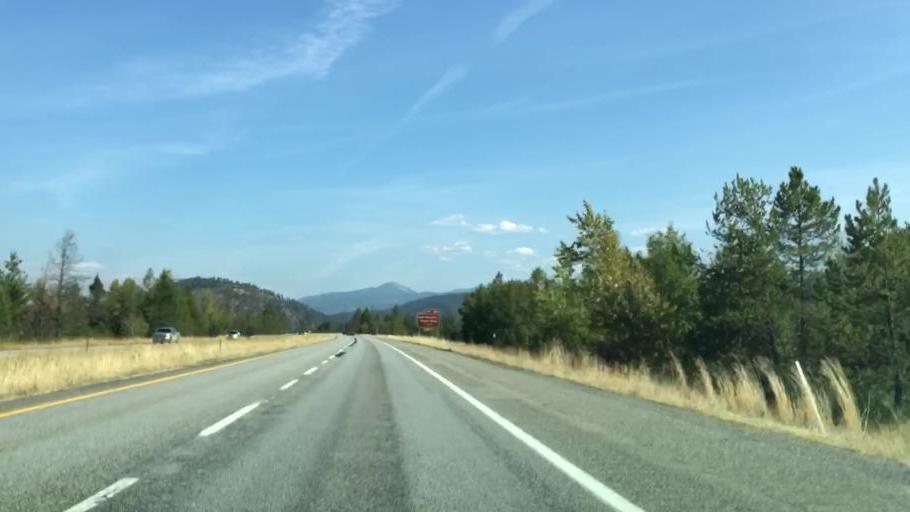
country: US
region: Idaho
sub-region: Shoshone County
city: Pinehurst
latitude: 47.5569
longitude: -116.3840
